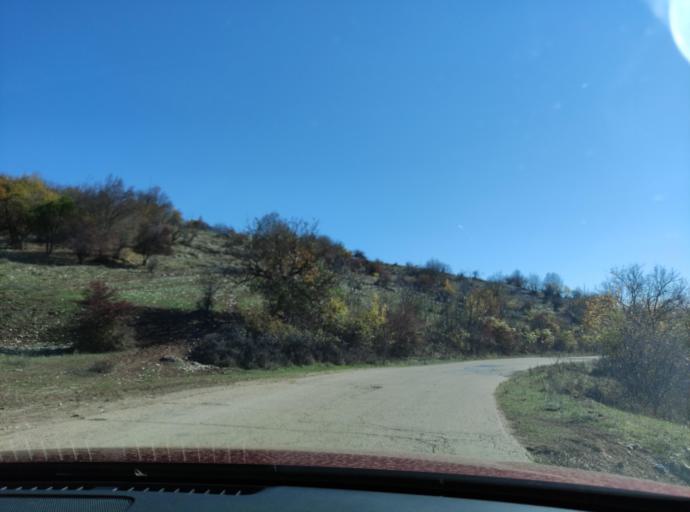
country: BG
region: Montana
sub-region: Obshtina Montana
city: Montana
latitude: 43.4405
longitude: 23.0531
